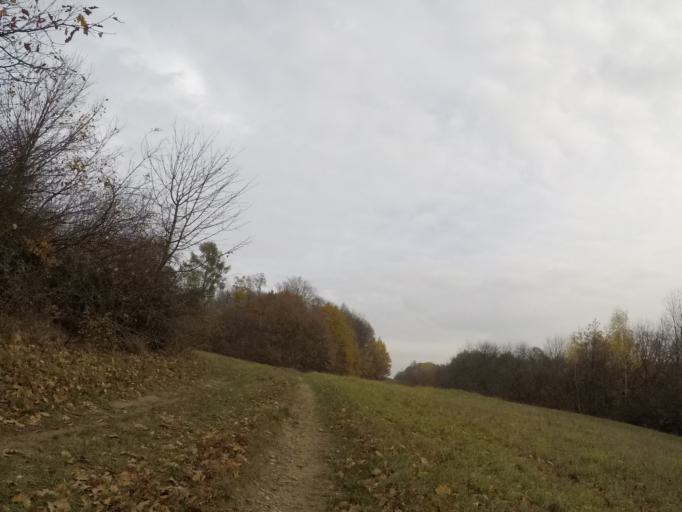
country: SK
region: Presovsky
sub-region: Okres Presov
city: Presov
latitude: 48.9414
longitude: 21.1415
